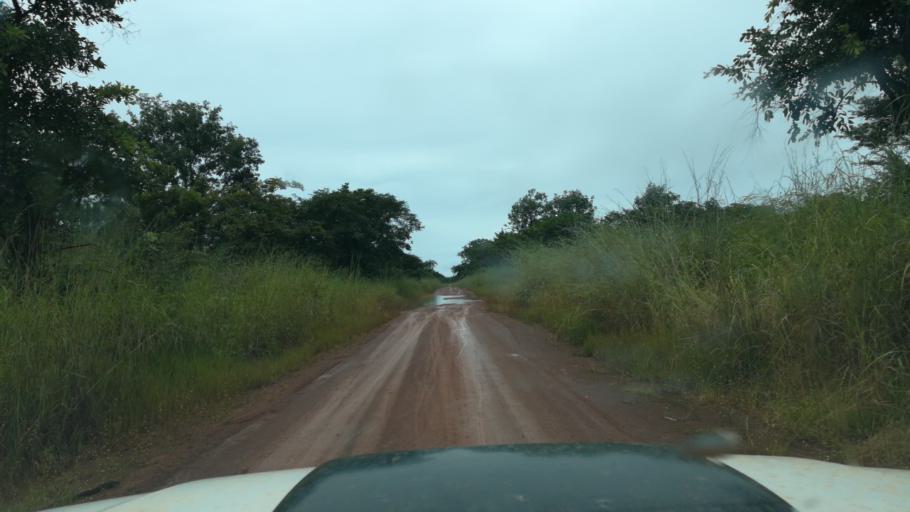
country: ZM
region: Luapula
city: Mwense
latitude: -10.1898
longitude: 28.1165
